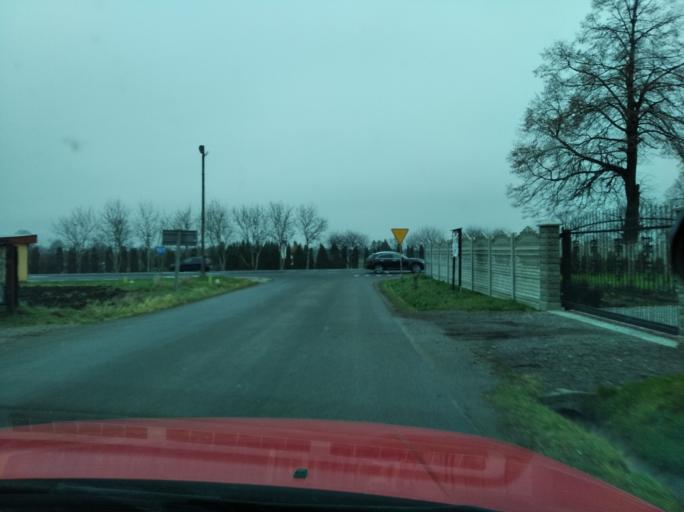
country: PL
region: Subcarpathian Voivodeship
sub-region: Powiat jaroslawski
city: Wierzbna
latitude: 50.0316
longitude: 22.6054
